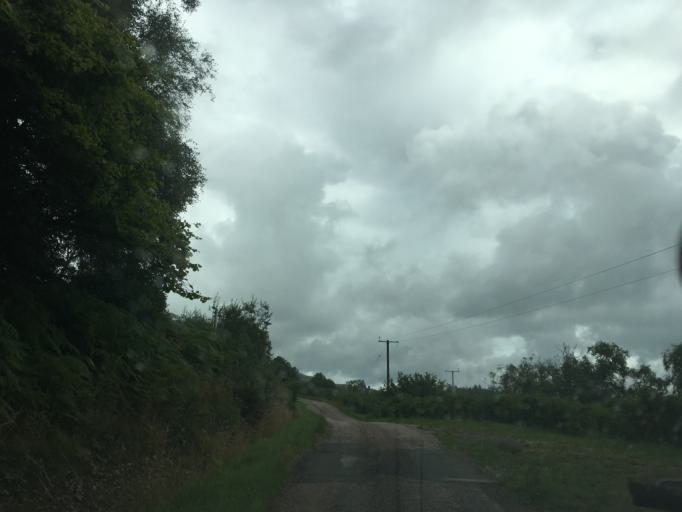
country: GB
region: Scotland
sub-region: Argyll and Bute
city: Oban
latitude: 56.2804
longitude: -5.3519
